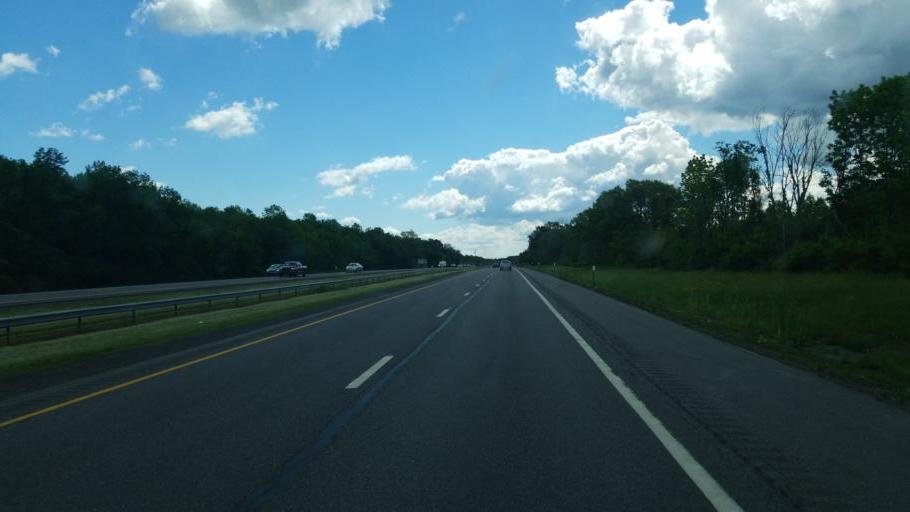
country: US
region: New York
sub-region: Madison County
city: Canastota
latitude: 43.0924
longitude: -75.7880
